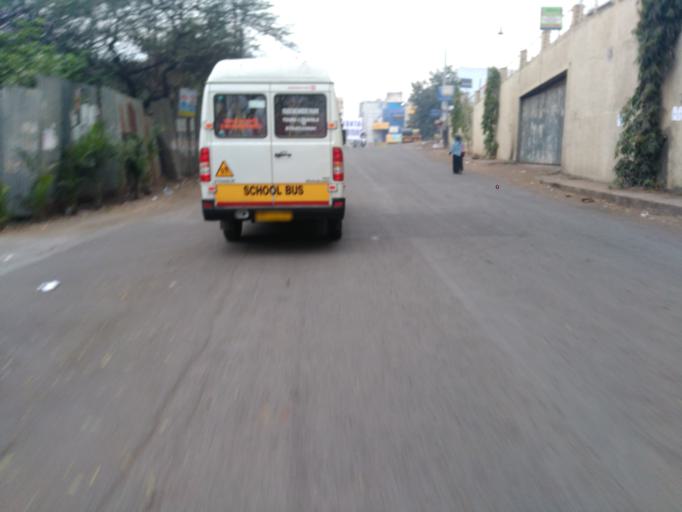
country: IN
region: Maharashtra
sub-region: Pune Division
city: Pune
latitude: 18.4624
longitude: 73.8891
